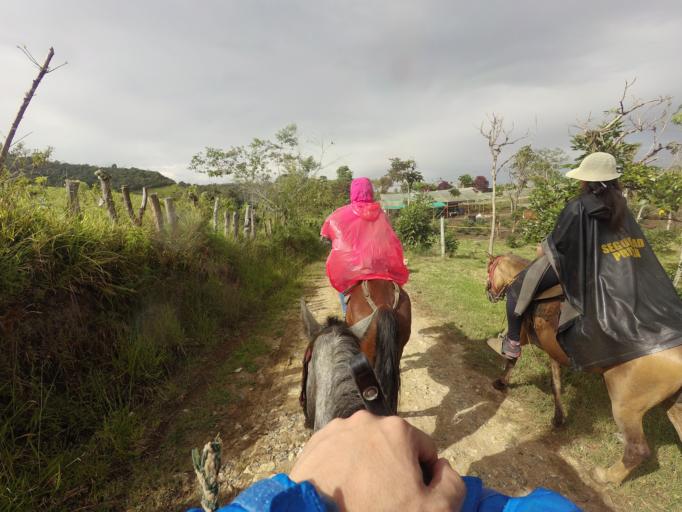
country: CO
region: Huila
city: San Agustin
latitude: 1.9114
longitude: -76.2921
